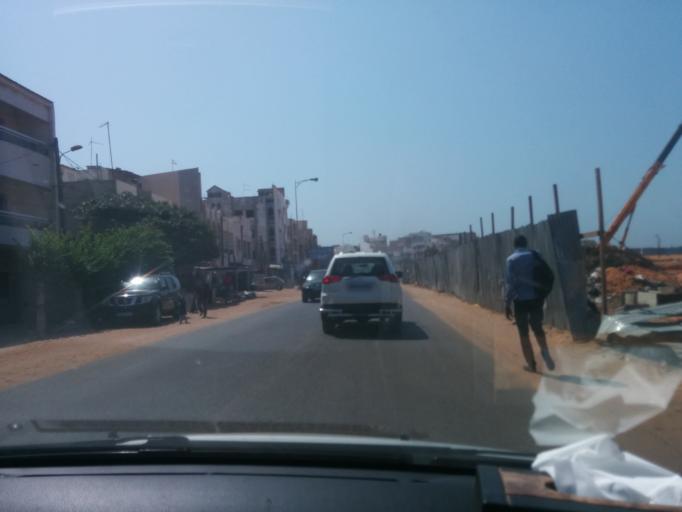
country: SN
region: Dakar
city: Grand Dakar
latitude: 14.7539
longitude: -17.4540
